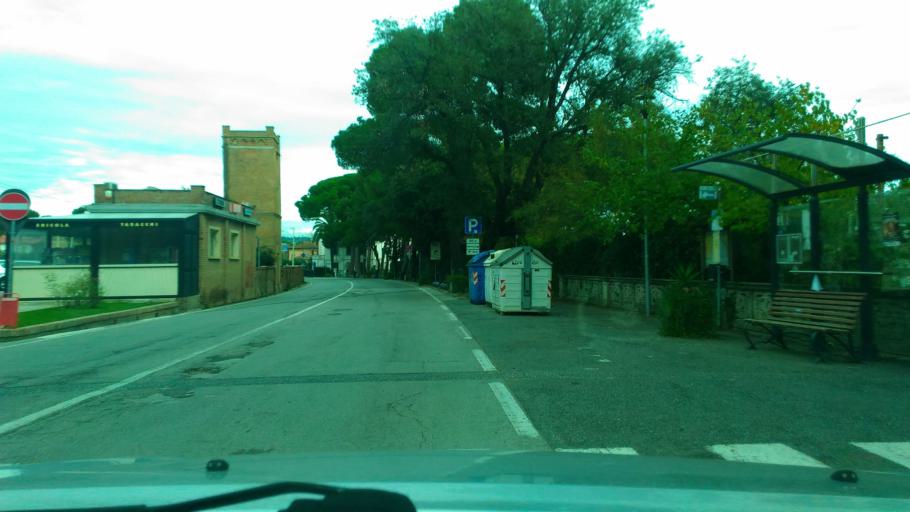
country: IT
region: Tuscany
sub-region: Provincia di Livorno
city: Rosignano Solvay-Castiglioncello
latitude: 43.4043
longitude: 10.4143
